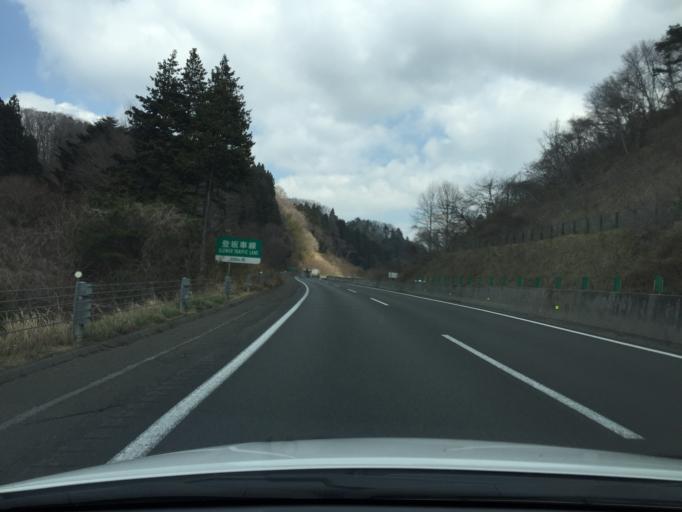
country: JP
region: Miyagi
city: Sendai
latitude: 38.2408
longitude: 140.8182
